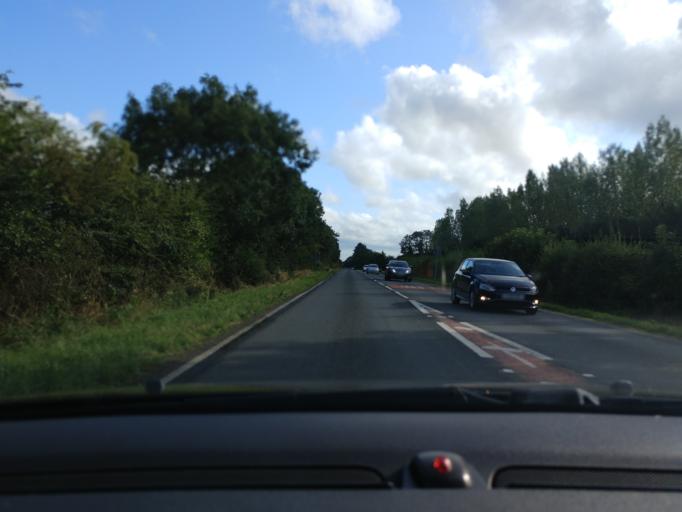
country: GB
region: England
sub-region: Oxfordshire
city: Bicester
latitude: 51.8828
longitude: -1.2291
